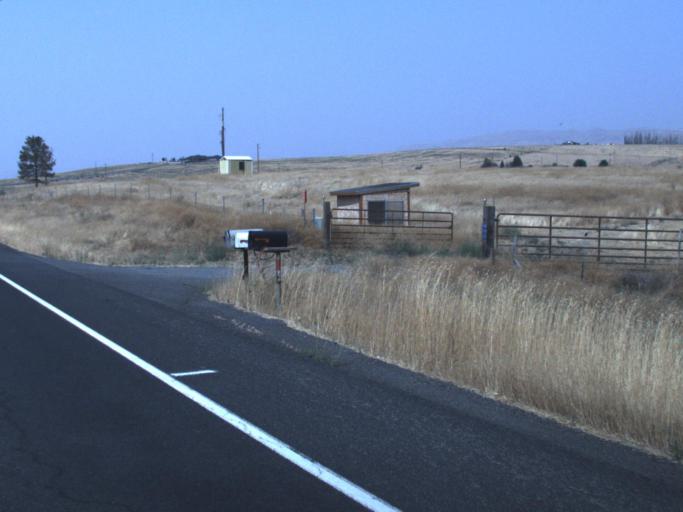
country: US
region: Washington
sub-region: Yakima County
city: Zillah
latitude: 46.5077
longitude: -120.1918
